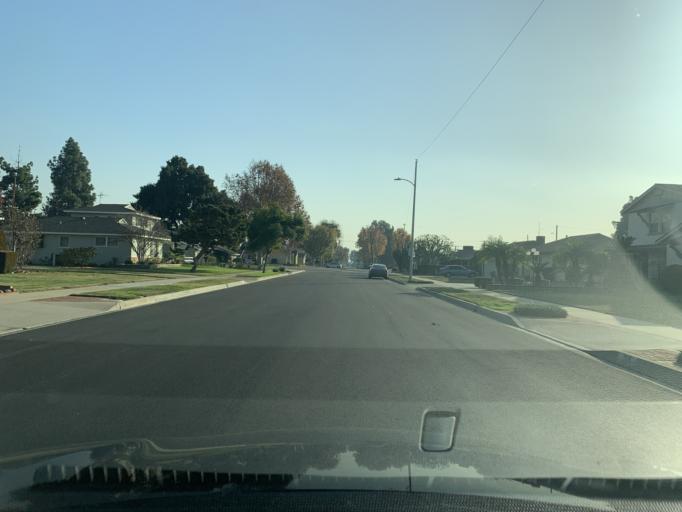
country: US
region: California
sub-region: Los Angeles County
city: Covina
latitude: 34.0874
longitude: -117.9012
